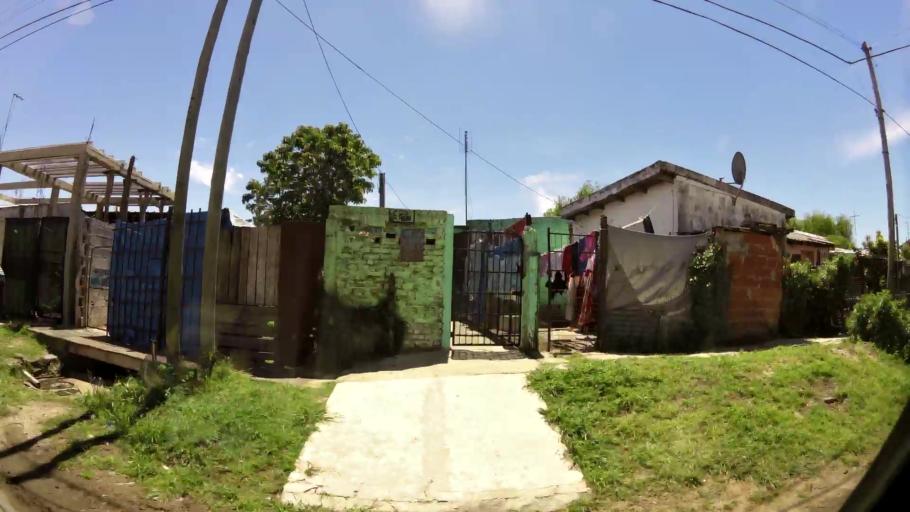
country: AR
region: Buenos Aires
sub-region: Partido de Quilmes
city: Quilmes
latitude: -34.7400
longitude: -58.3165
